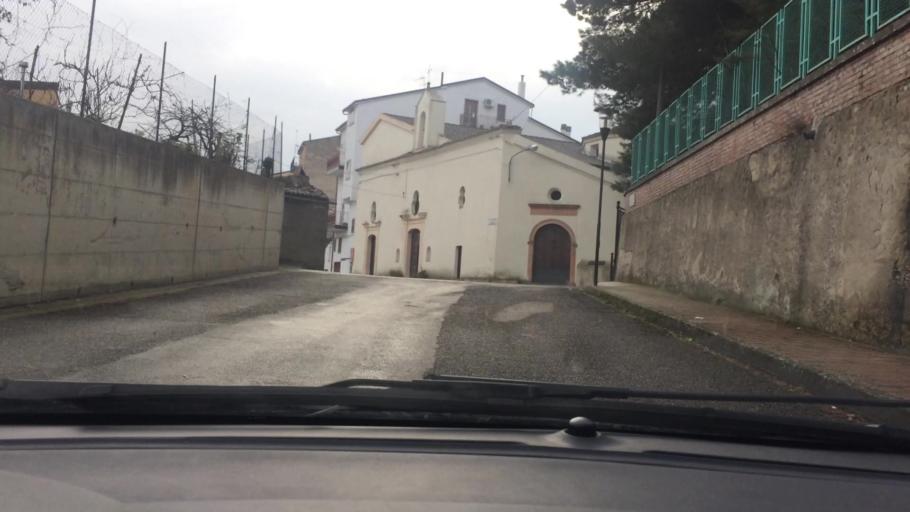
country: IT
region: Basilicate
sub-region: Provincia di Matera
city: San Mauro Forte
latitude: 40.4880
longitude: 16.2465
